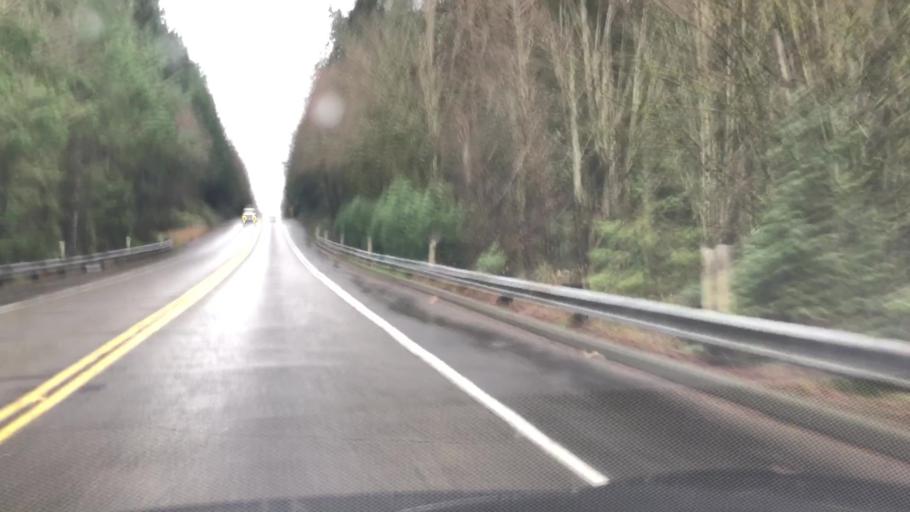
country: US
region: Washington
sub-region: King County
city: Redmond
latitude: 47.7126
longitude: -122.1156
